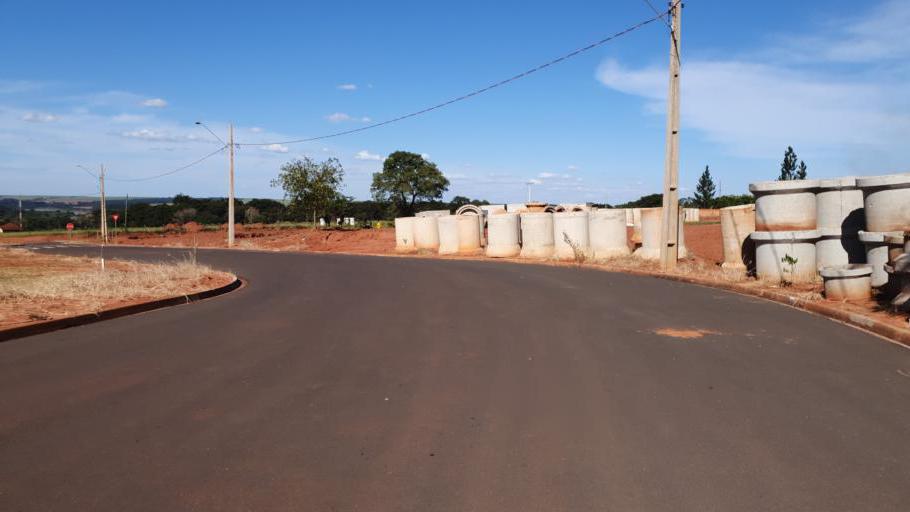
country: BR
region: Sao Paulo
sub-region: Paraguacu Paulista
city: Paraguacu Paulista
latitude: -22.3985
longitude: -50.5751
